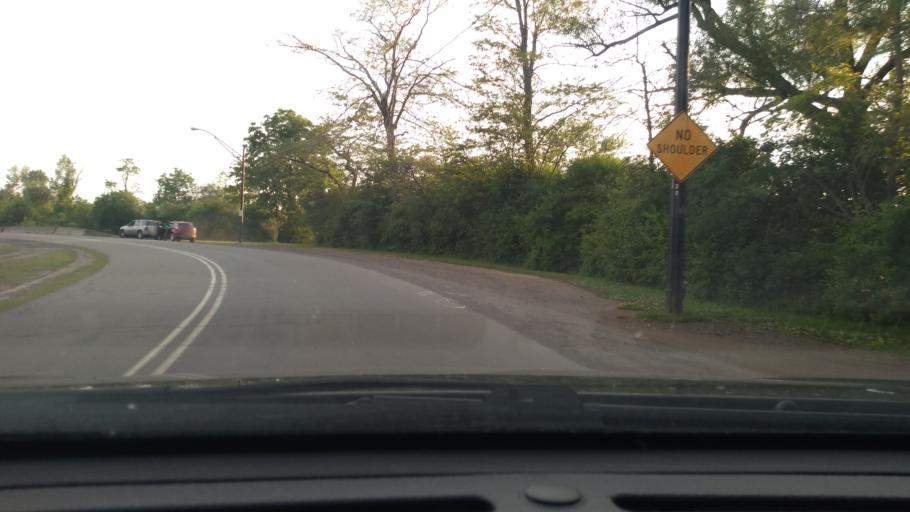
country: US
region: New York
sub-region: Erie County
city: Lackawanna
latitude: 42.8314
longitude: -78.8343
